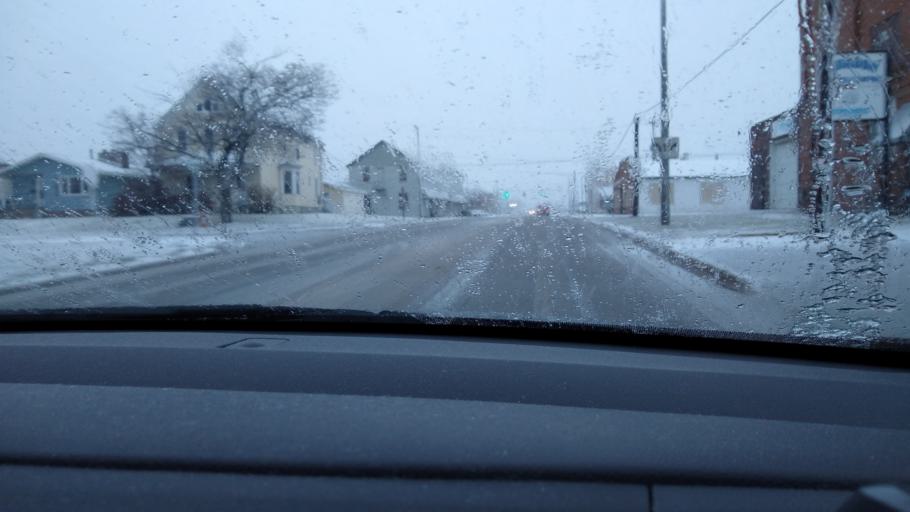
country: US
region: Michigan
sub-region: Delta County
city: Escanaba
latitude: 45.7493
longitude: -87.0698
